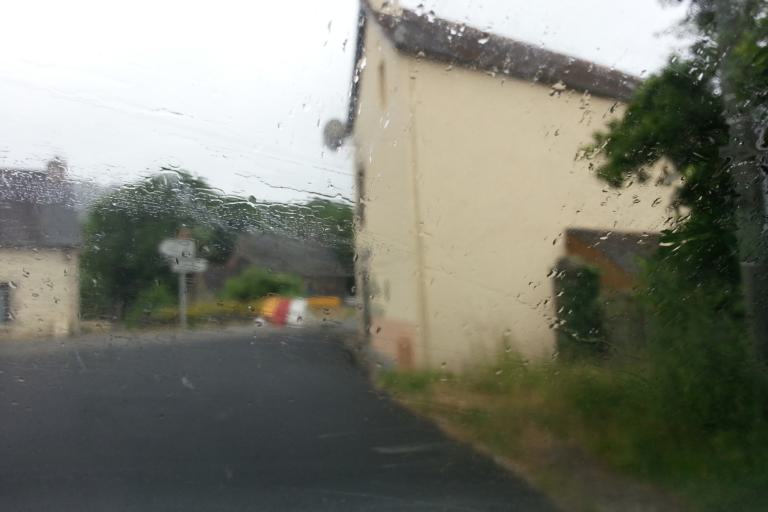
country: FR
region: Brittany
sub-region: Departement des Cotes-d'Armor
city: Gouarec
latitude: 48.2151
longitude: -3.1275
